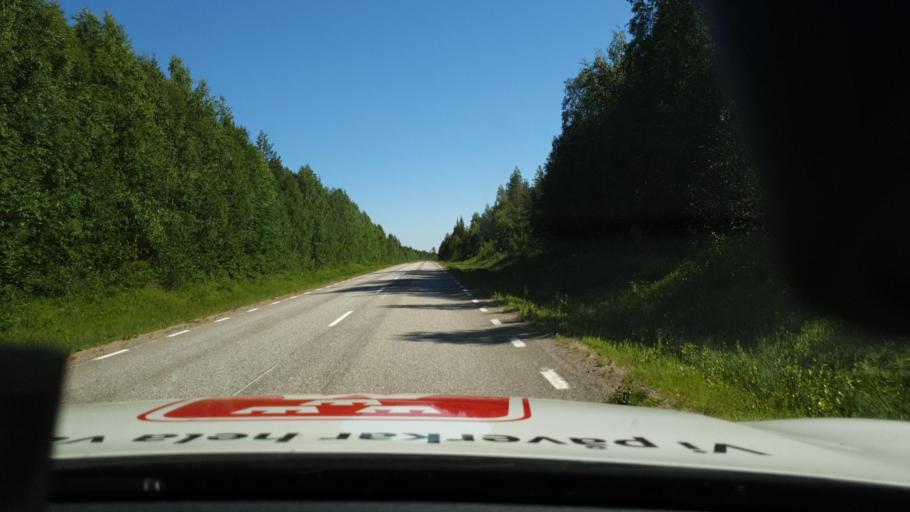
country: SE
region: Norrbotten
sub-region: Lulea Kommun
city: Ranea
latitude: 66.0055
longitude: 22.3200
